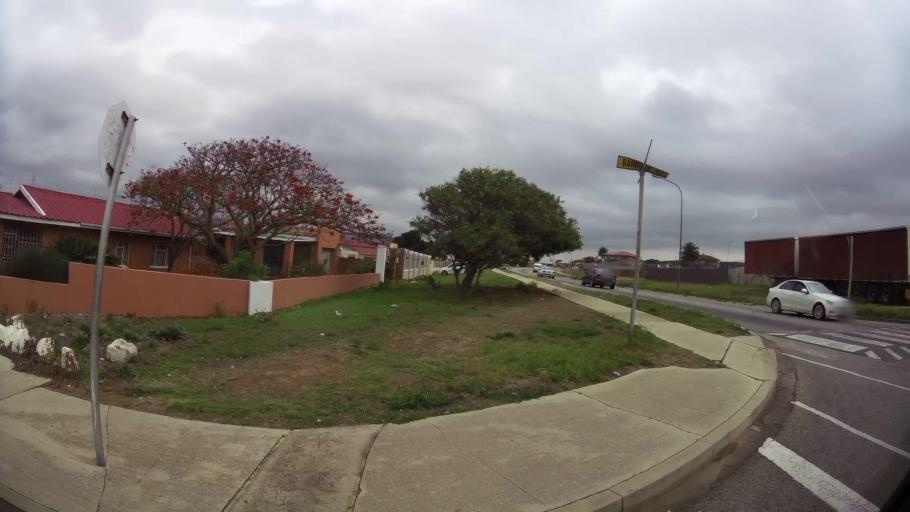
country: ZA
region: Eastern Cape
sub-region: Nelson Mandela Bay Metropolitan Municipality
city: Port Elizabeth
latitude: -33.9078
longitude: 25.5669
